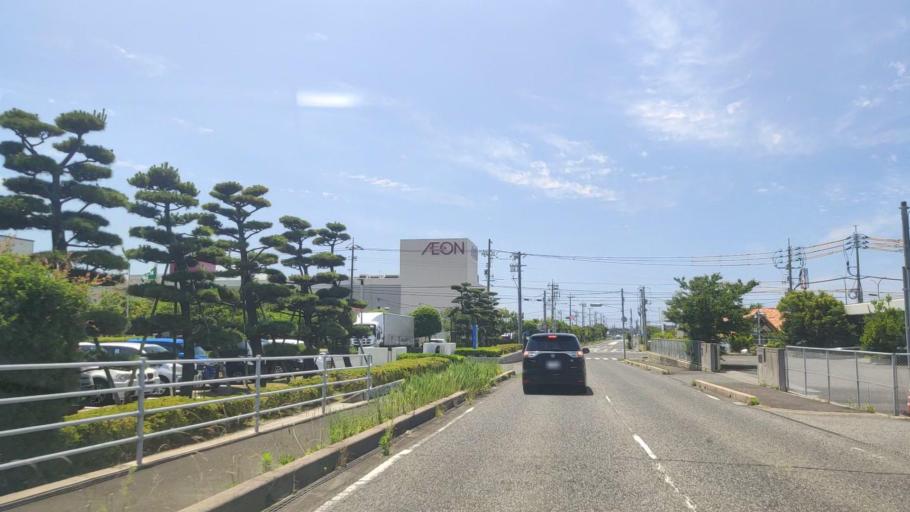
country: JP
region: Tottori
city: Tottori
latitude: 35.5253
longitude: 134.2039
